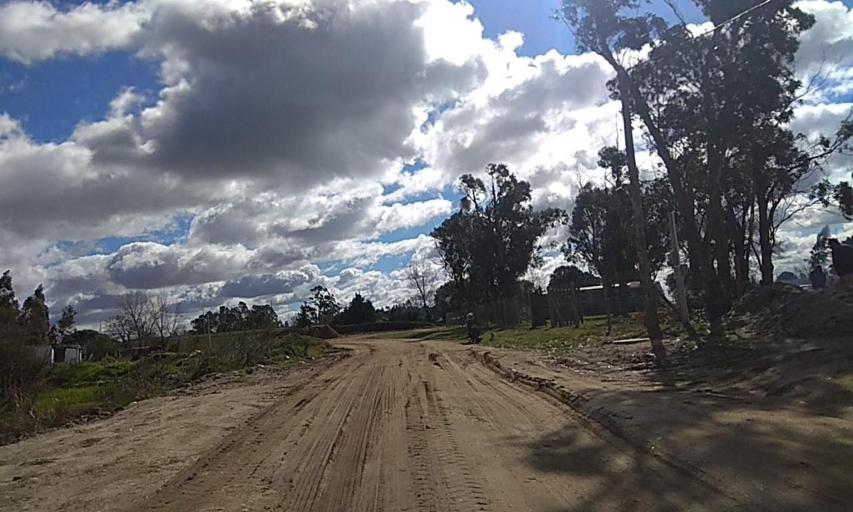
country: UY
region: Florida
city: Florida
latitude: -34.0793
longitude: -56.2273
